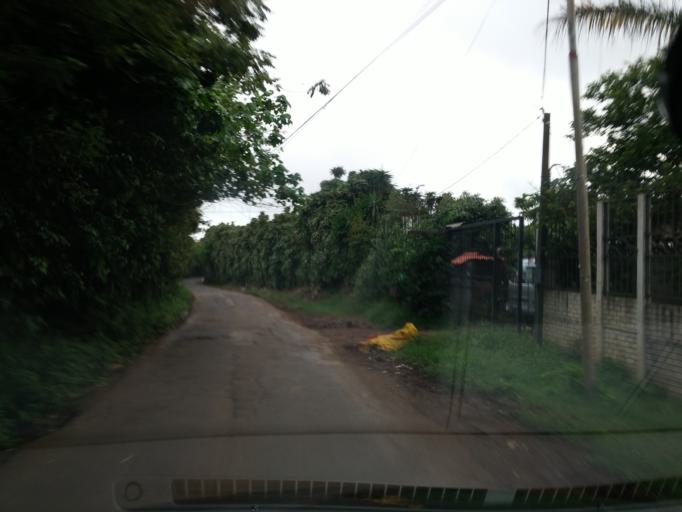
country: CR
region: Heredia
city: San Josecito
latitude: 10.0283
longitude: -84.0977
